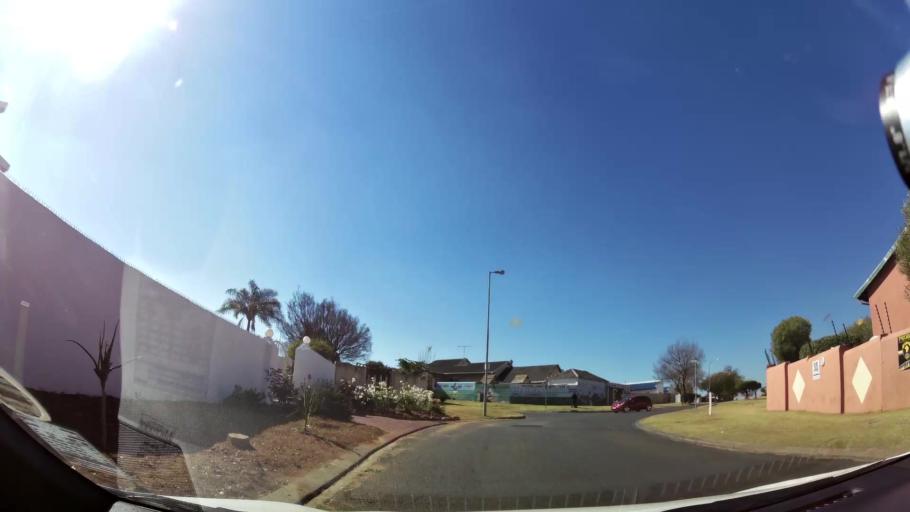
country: ZA
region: Gauteng
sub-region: City of Johannesburg Metropolitan Municipality
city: Johannesburg
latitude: -26.2638
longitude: 27.9924
